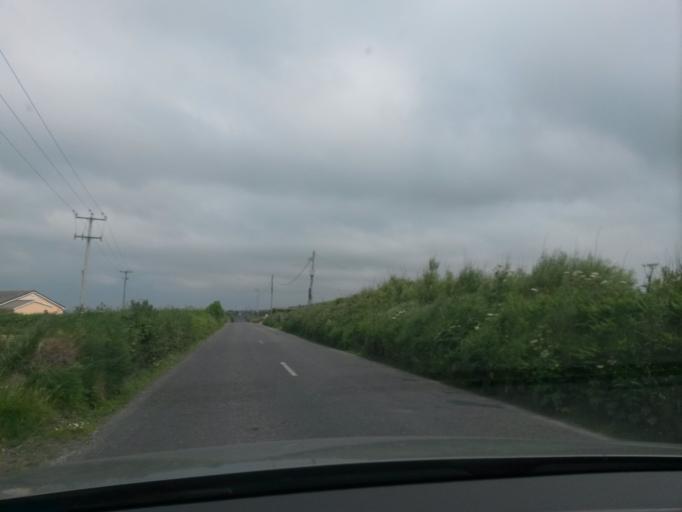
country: IE
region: Munster
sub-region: Ciarrai
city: Ballybunnion
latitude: 52.5269
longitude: -9.6617
